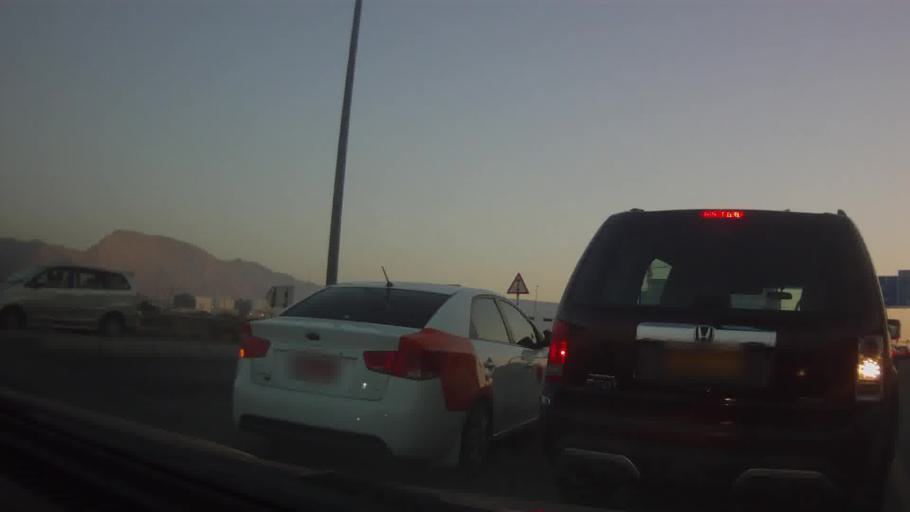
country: OM
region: Muhafazat Masqat
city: Bawshar
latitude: 23.5891
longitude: 58.4147
